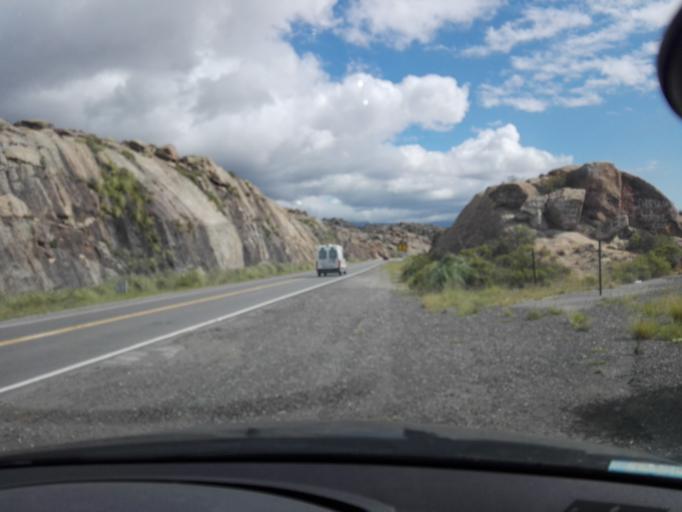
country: AR
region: Cordoba
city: Mina Clavero
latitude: -31.7567
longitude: -64.9129
